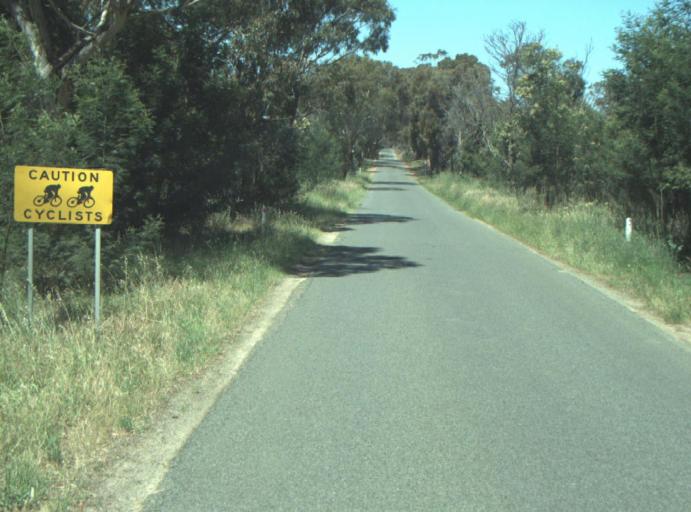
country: AU
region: Victoria
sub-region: Moorabool
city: Bacchus Marsh
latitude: -37.8311
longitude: 144.2887
